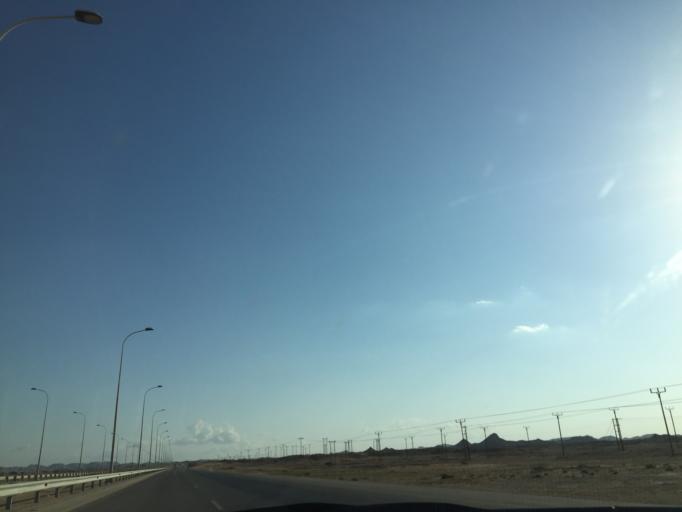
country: OM
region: Zufar
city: Salalah
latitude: 17.5276
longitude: 54.0557
